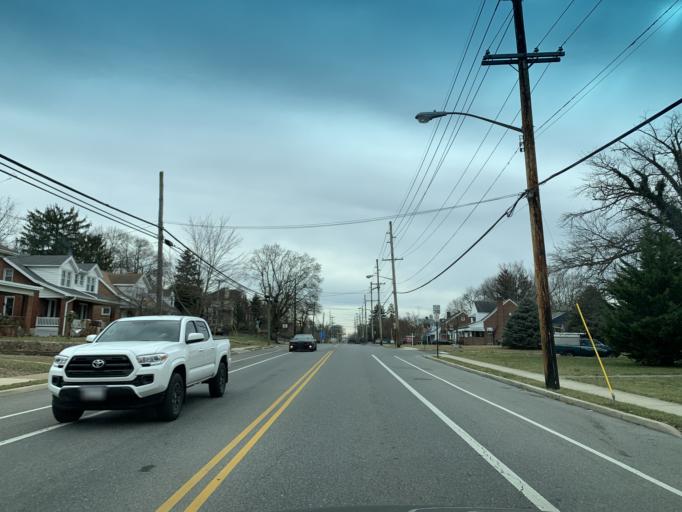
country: US
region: Maryland
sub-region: Washington County
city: Hagerstown
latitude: 39.6238
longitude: -77.7142
